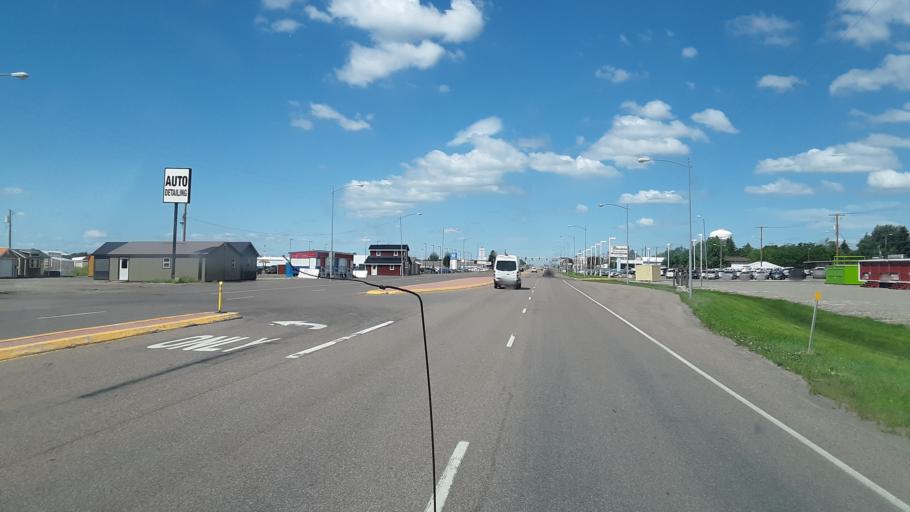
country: US
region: Montana
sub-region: Cascade County
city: Malmstrom Air Force Base
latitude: 47.4939
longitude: -111.2213
